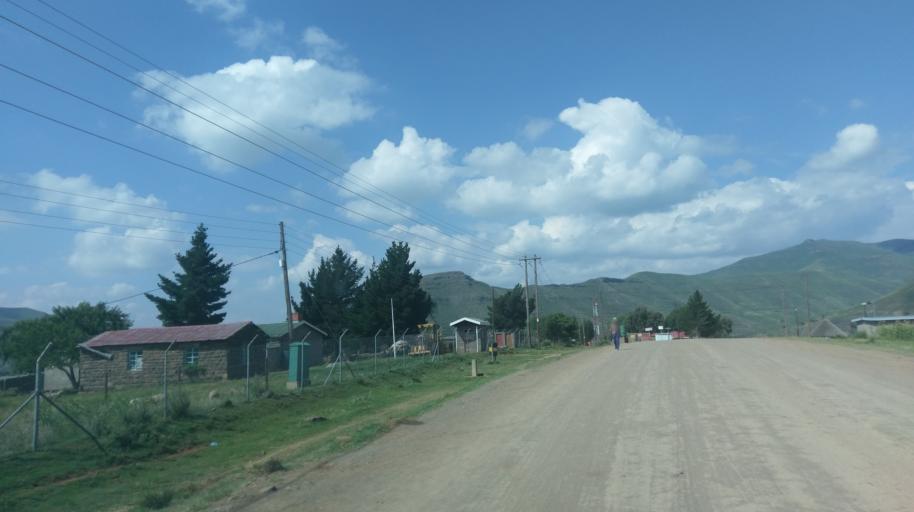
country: LS
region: Butha-Buthe
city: Butha-Buthe
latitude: -29.1065
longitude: 28.4959
